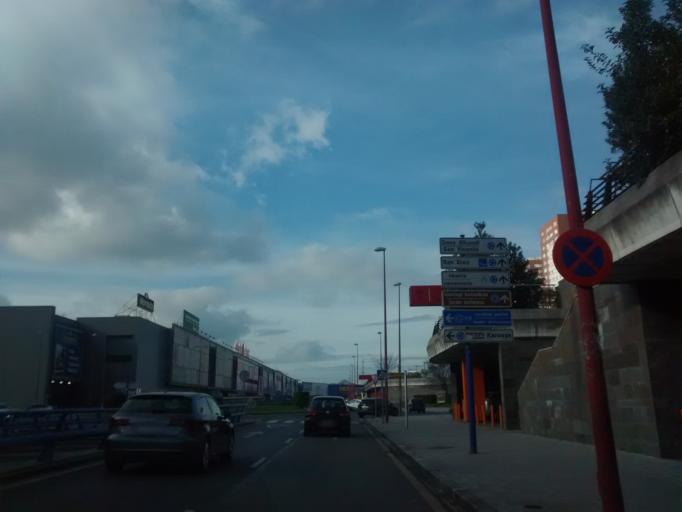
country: ES
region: Basque Country
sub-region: Bizkaia
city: Barakaldo
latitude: 43.2886
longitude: -3.0004
